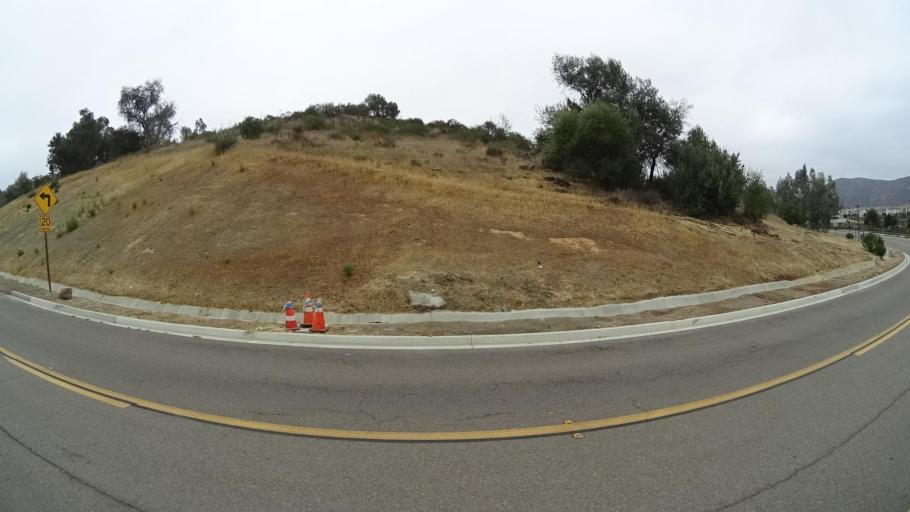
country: US
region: California
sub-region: San Diego County
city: Escondido
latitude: 33.1084
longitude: -117.1287
